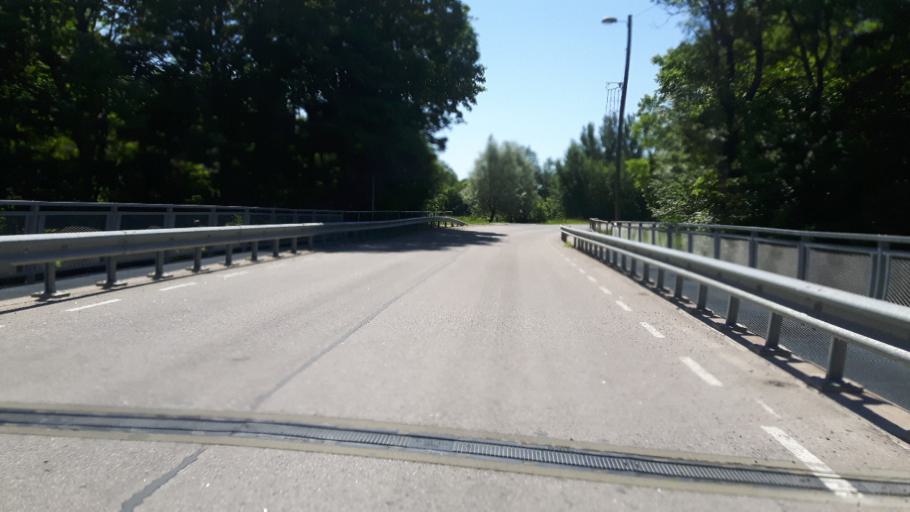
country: EE
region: Paernumaa
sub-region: Tootsi vald
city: Tootsi
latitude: 58.4936
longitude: 24.9010
